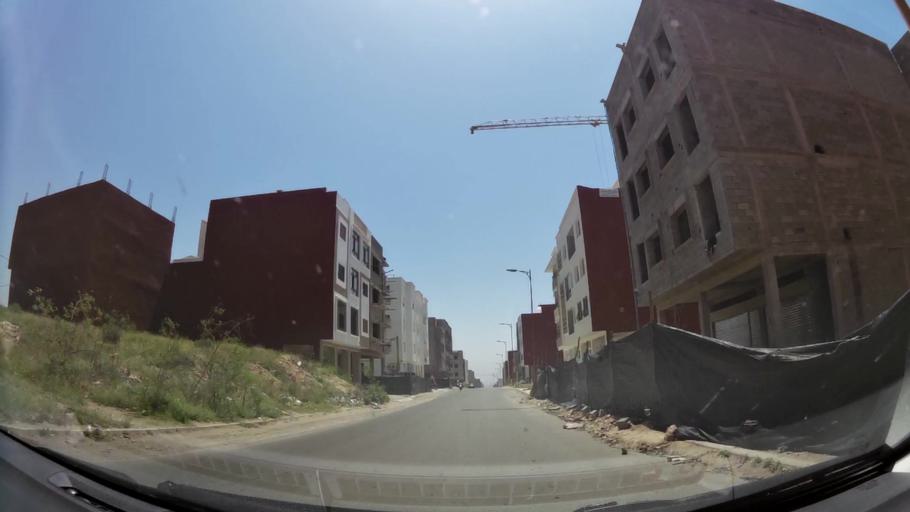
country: MA
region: Oued ed Dahab-Lagouira
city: Dakhla
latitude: 30.4425
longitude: -9.5568
